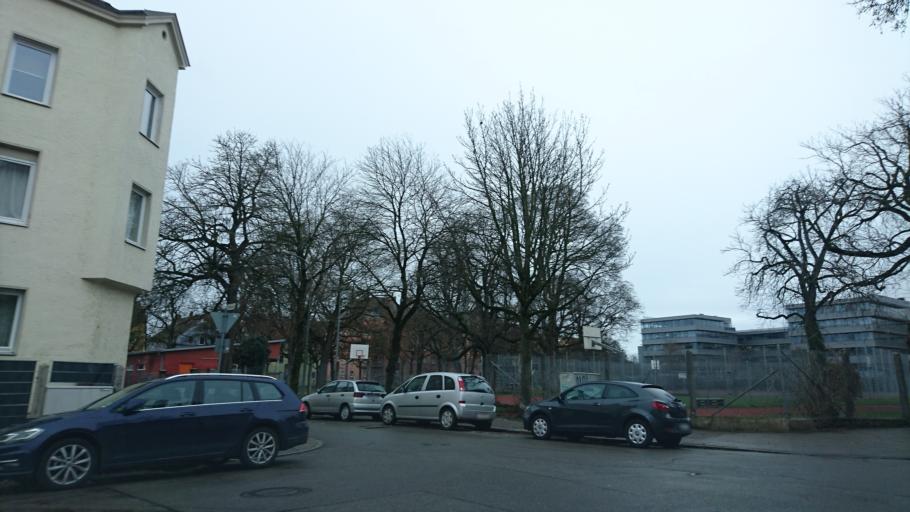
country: DE
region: Bavaria
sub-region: Swabia
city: Augsburg
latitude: 48.3806
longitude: 10.8875
